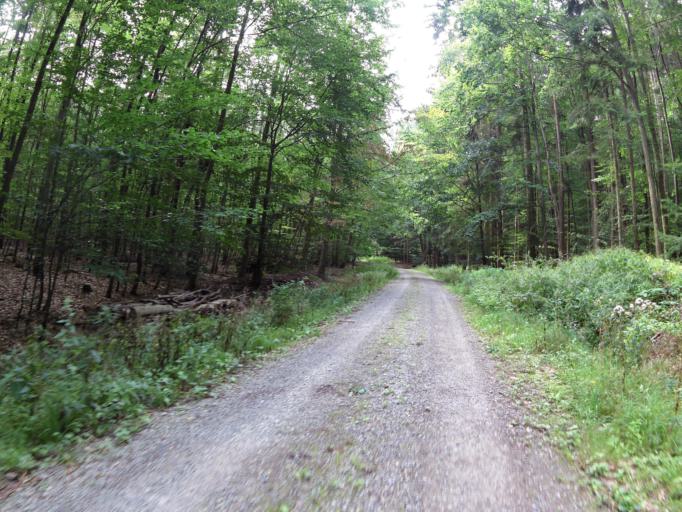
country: DE
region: Bavaria
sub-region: Regierungsbezirk Unterfranken
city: Kist
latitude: 49.7216
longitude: 9.8177
